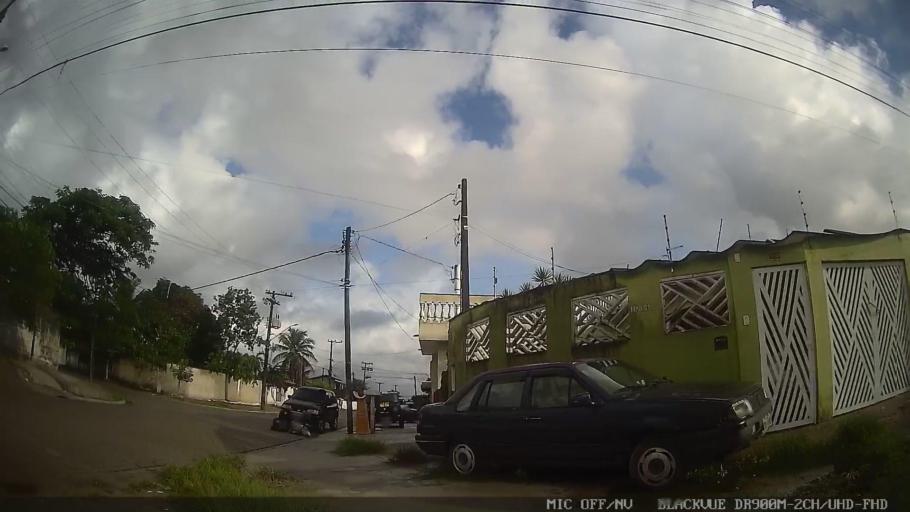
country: BR
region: Sao Paulo
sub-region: Itanhaem
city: Itanhaem
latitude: -24.1805
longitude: -46.8546
